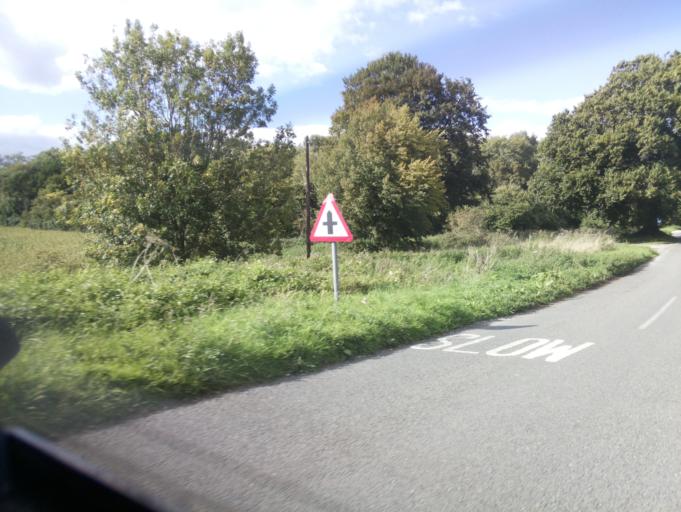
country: GB
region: England
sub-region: Hampshire
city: Chandlers Ford
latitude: 51.0603
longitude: -1.3811
